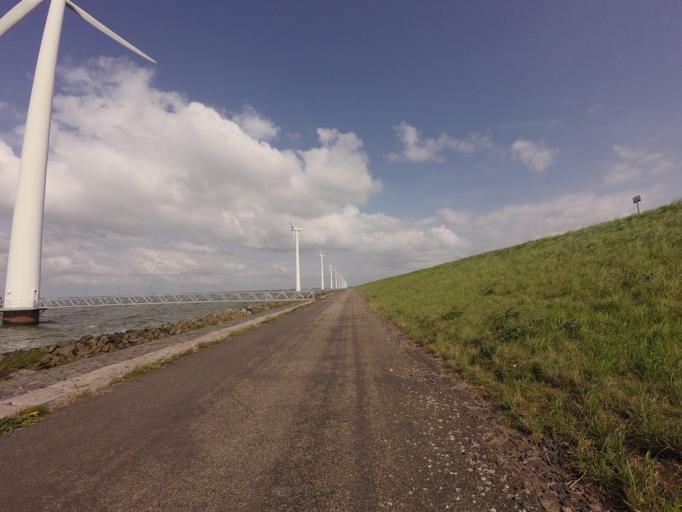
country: NL
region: Flevoland
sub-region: Gemeente Urk
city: Urk
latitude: 52.5978
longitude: 5.5838
